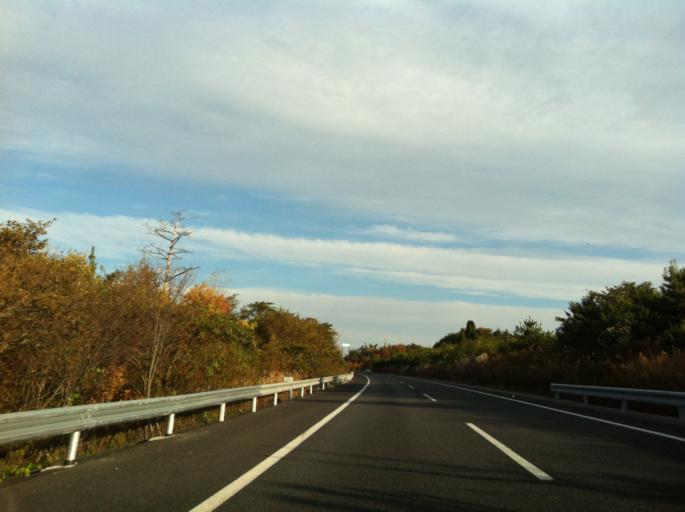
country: JP
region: Gifu
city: Toki
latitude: 35.2998
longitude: 137.1807
